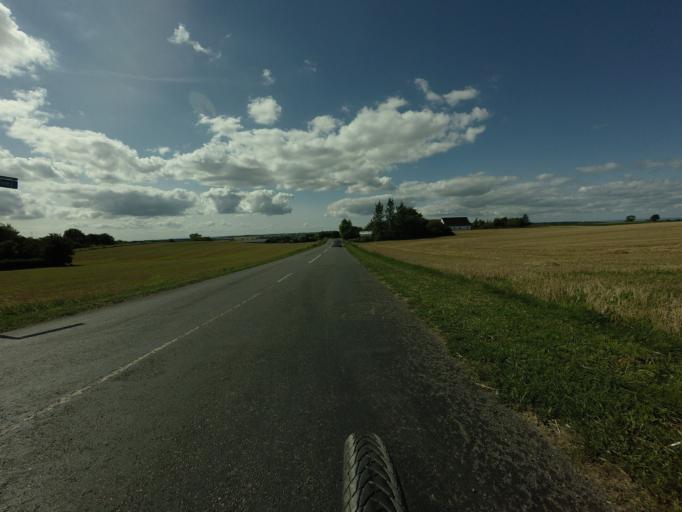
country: DK
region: Zealand
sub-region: Vordingborg Kommune
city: Stege
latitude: 54.9945
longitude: 12.4885
